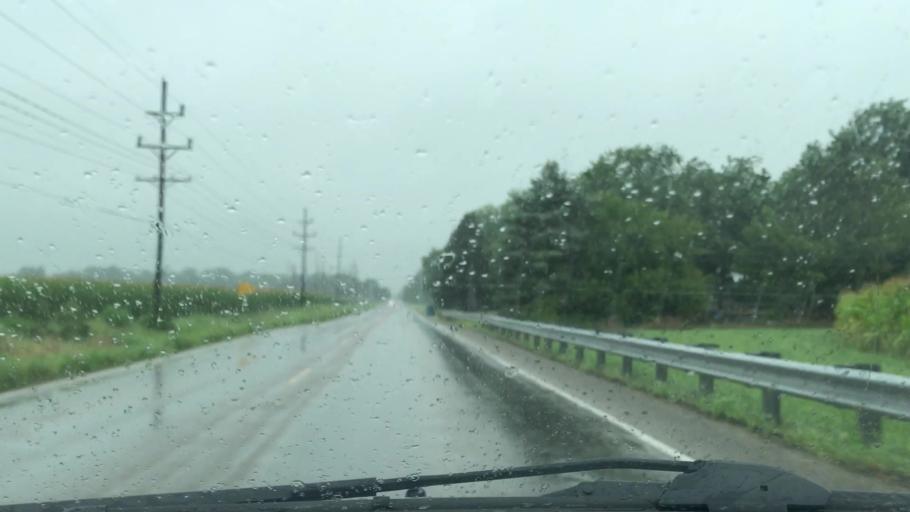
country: US
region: Indiana
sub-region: Hamilton County
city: Sheridan
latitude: 40.1138
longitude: -86.1726
